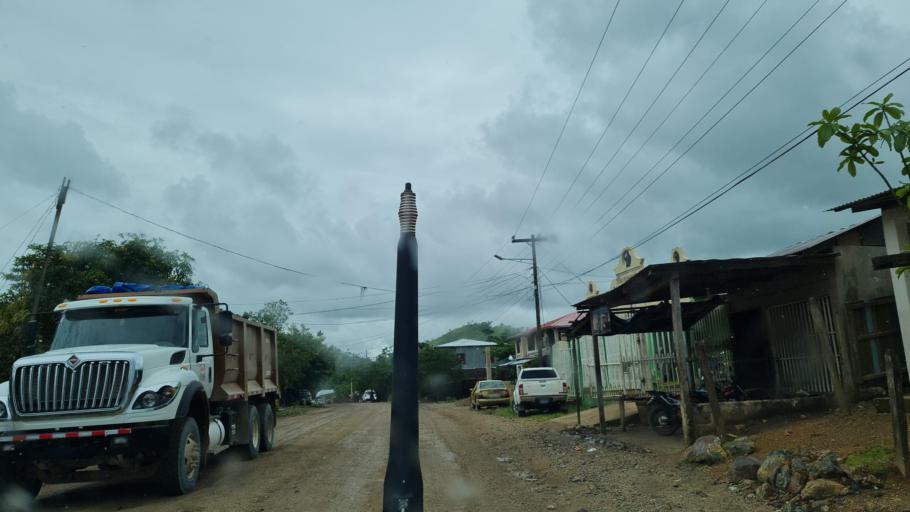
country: NI
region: Atlantico Norte (RAAN)
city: Bonanza
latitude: 13.9197
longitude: -84.3912
